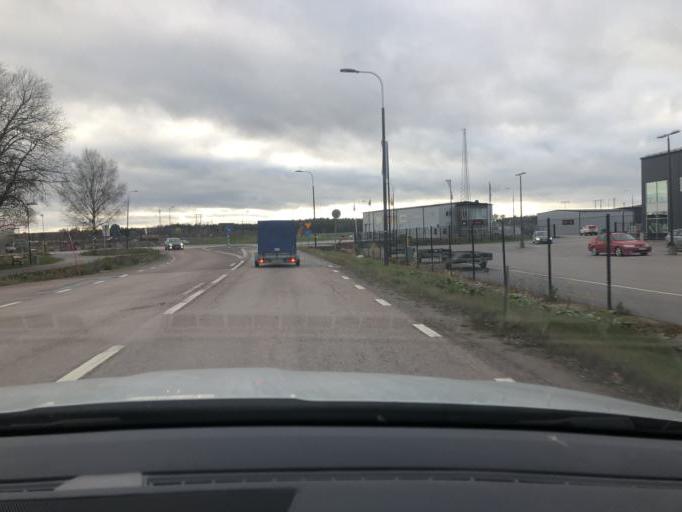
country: SE
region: Uppsala
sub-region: Tierps Kommun
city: Tierp
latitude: 60.3465
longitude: 17.4925
